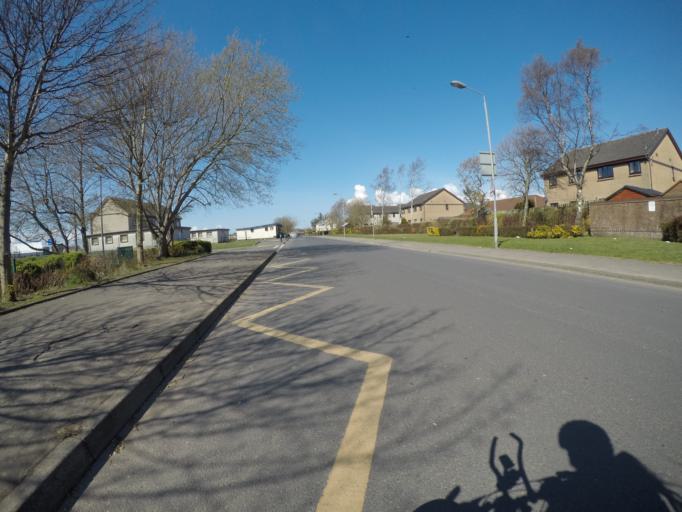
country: GB
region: Scotland
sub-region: North Ayrshire
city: Irvine
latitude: 55.6199
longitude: -4.6592
